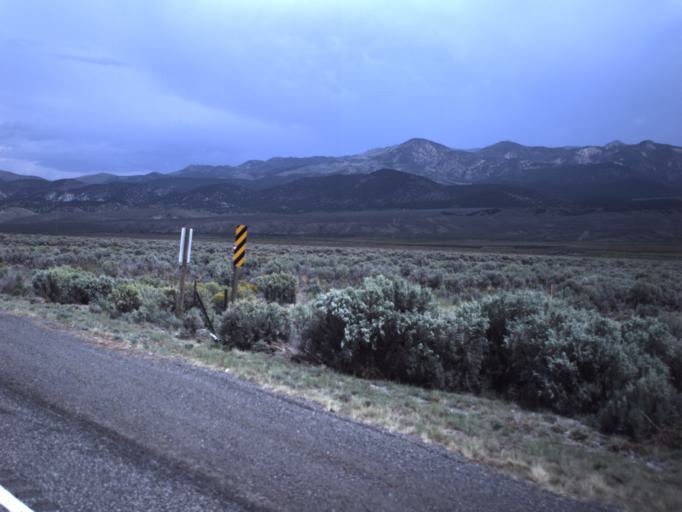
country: US
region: Utah
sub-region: Garfield County
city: Panguitch
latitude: 37.9880
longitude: -112.3949
